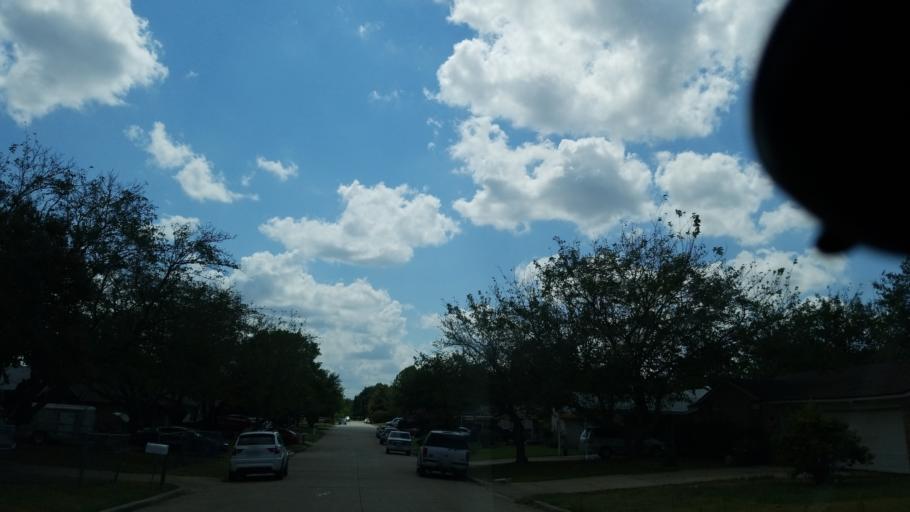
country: US
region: Texas
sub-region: Dallas County
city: Grand Prairie
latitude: 32.7195
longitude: -96.9831
